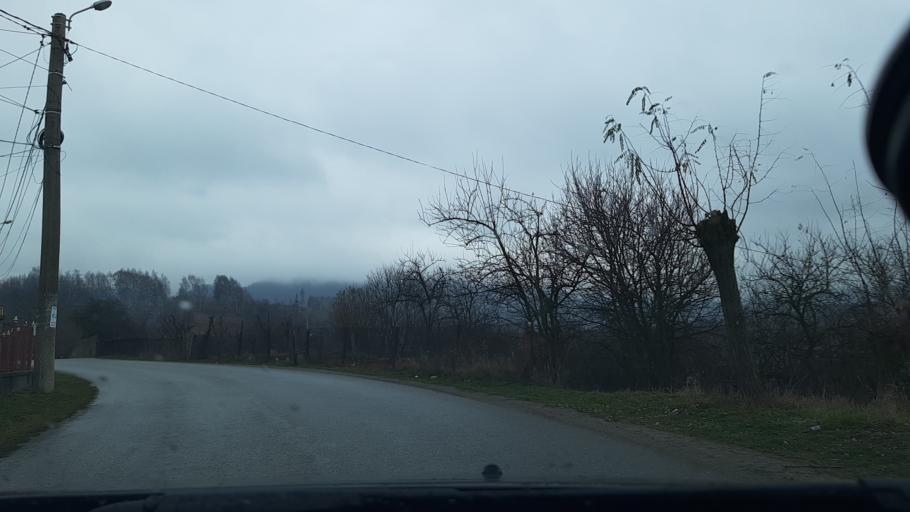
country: RO
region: Hunedoara
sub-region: Oras Petrila
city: Petrila
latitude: 45.4402
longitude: 23.4117
